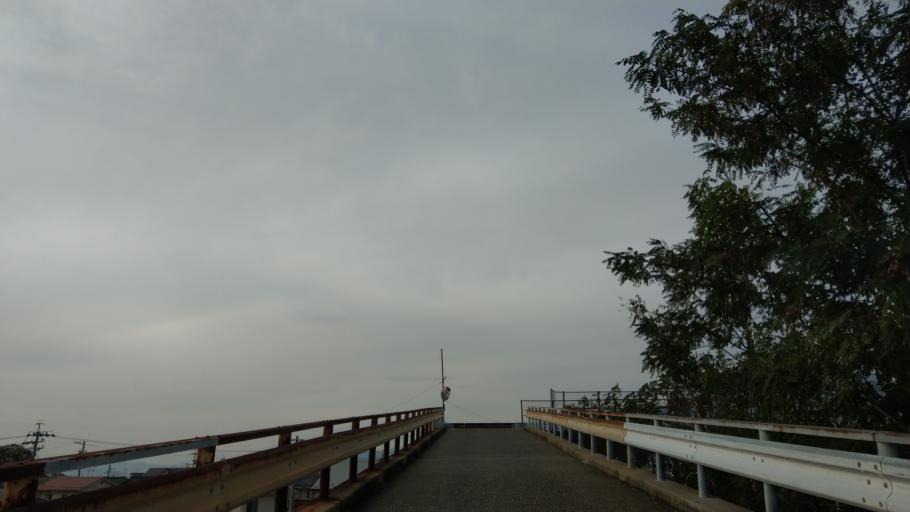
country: JP
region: Nagano
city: Komoro
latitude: 36.3207
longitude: 138.4282
